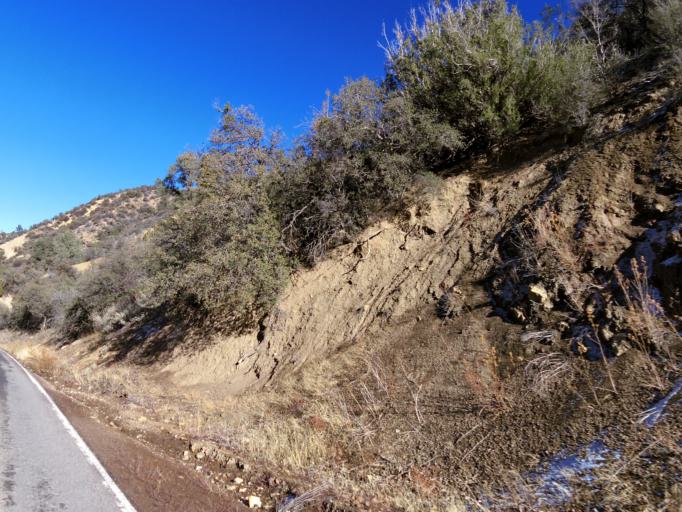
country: US
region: California
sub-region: Ventura County
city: Meiners Oaks
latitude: 34.6715
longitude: -119.3727
